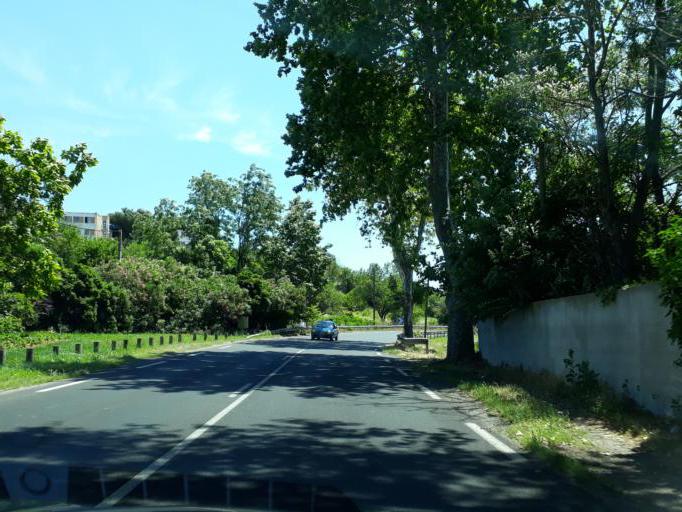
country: FR
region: Languedoc-Roussillon
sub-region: Departement de l'Herault
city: Beziers
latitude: 43.3264
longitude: 3.2456
